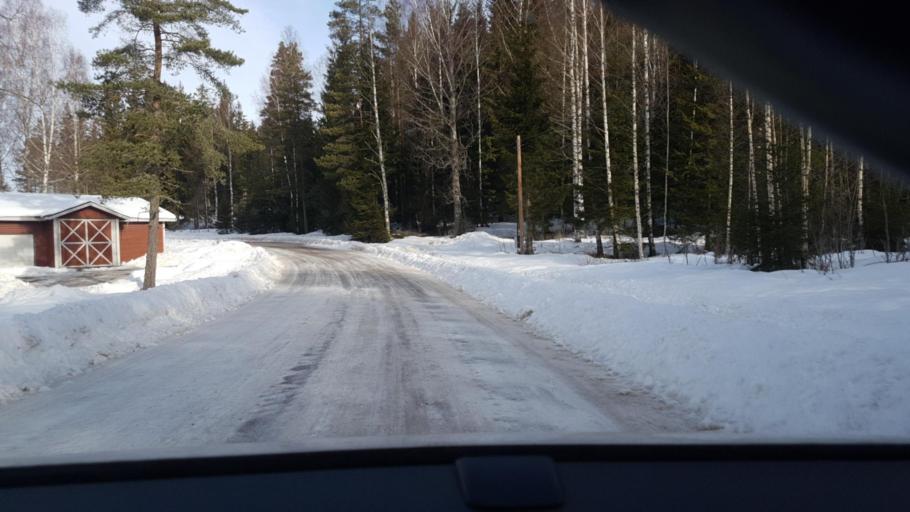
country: NO
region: Ostfold
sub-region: Romskog
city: Romskog
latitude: 59.8321
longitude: 11.9867
